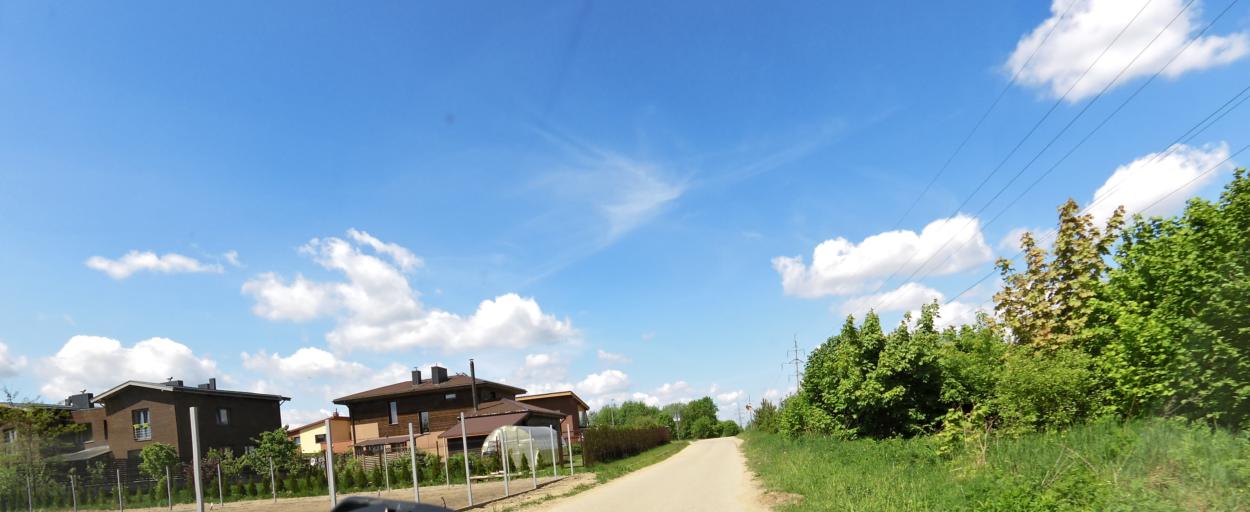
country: LT
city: Lentvaris
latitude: 54.6339
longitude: 25.0815
